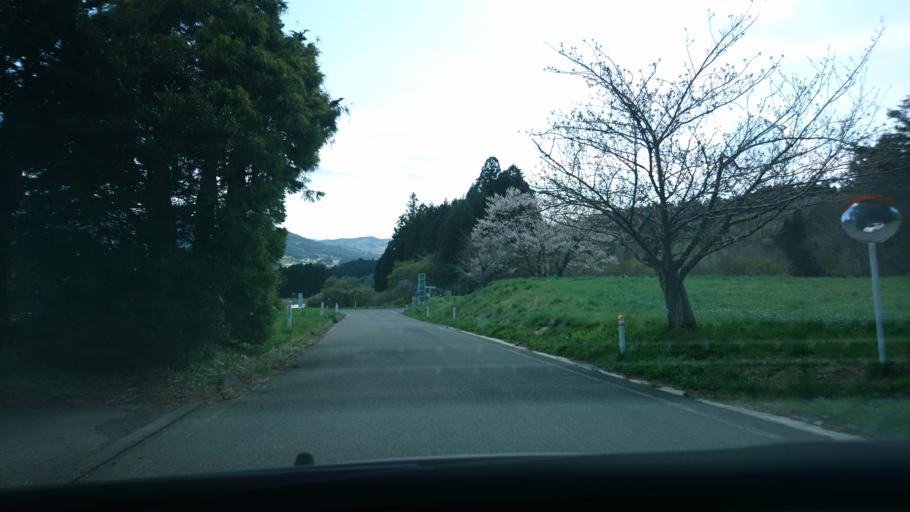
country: JP
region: Iwate
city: Ofunato
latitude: 38.9542
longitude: 141.4518
